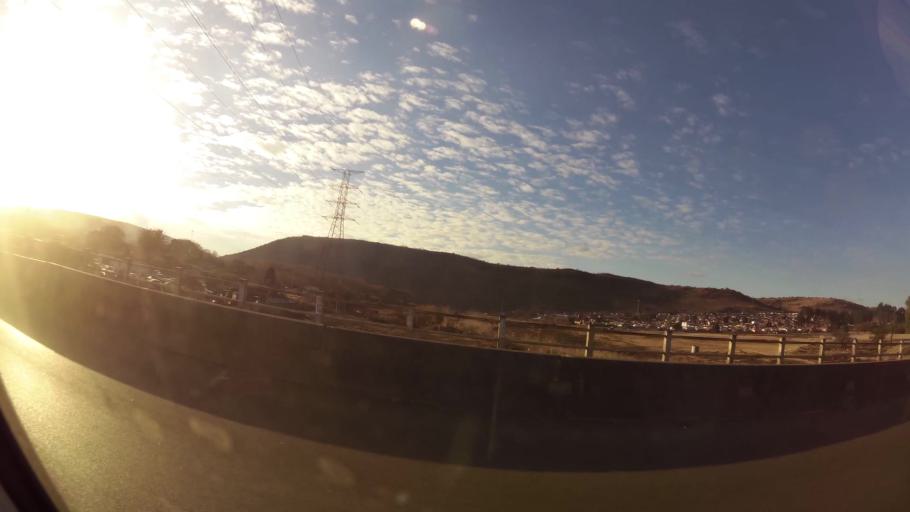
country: ZA
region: Gauteng
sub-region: City of Tshwane Metropolitan Municipality
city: Cullinan
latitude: -25.7105
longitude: 28.3683
